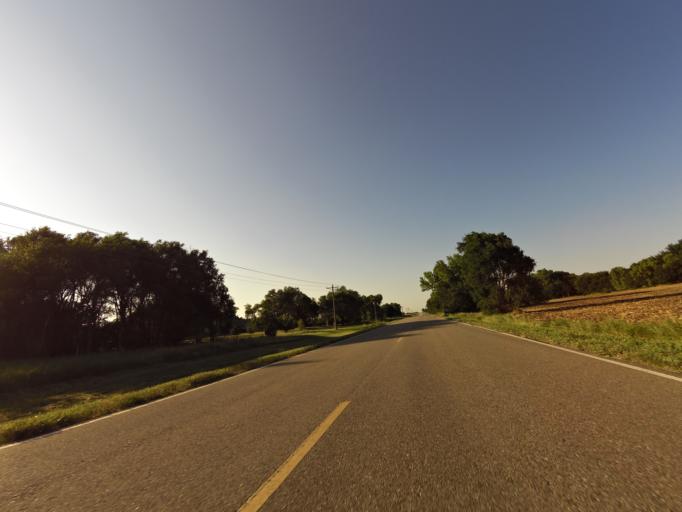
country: US
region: Kansas
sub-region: Reno County
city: Buhler
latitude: 38.1696
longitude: -97.8486
